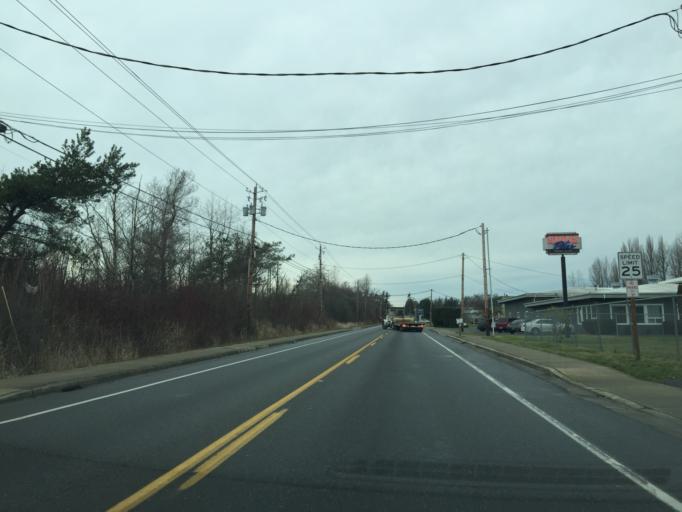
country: US
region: Washington
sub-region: Whatcom County
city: Bellingham
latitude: 48.7693
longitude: -122.5213
